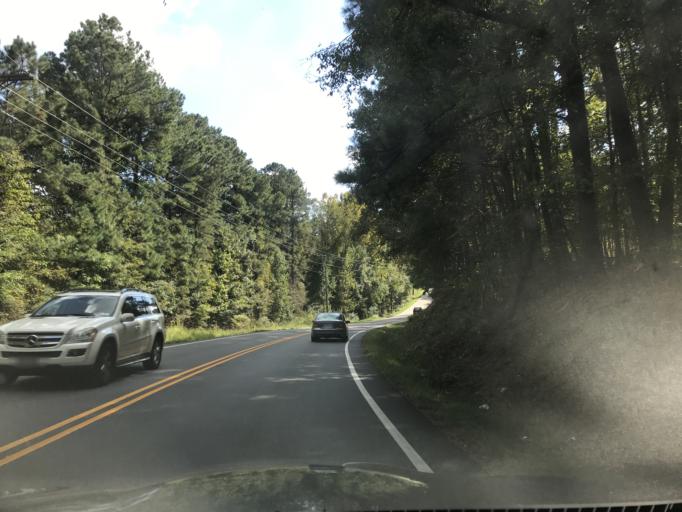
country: US
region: North Carolina
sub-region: Wake County
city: Rolesville
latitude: 35.9074
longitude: -78.5255
